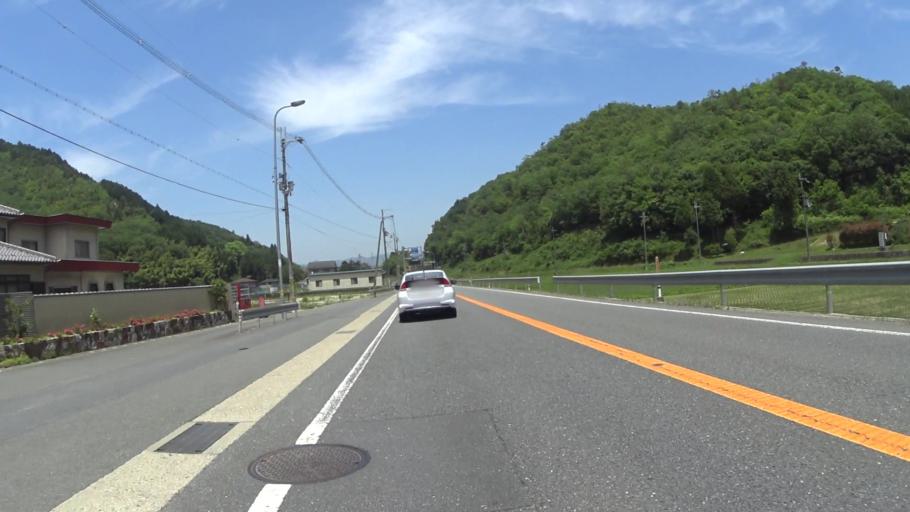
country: JP
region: Kyoto
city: Kameoka
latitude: 35.1417
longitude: 135.4262
